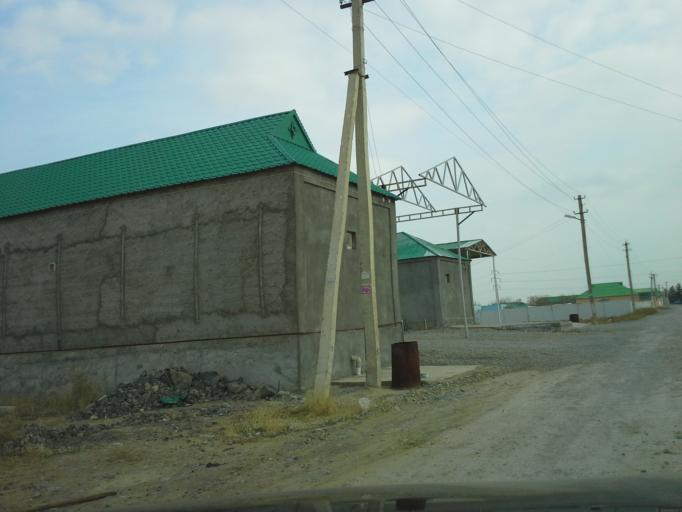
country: TM
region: Ahal
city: Abadan
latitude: 38.0381
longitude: 58.2509
